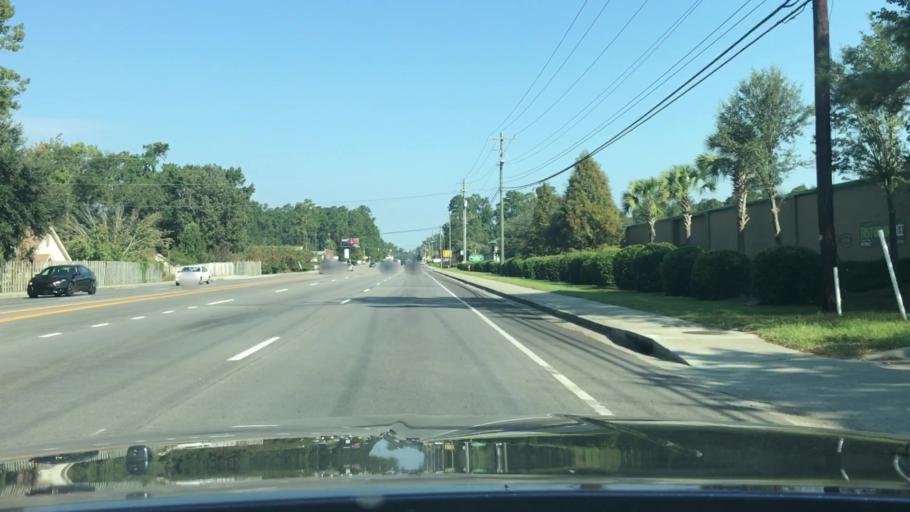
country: US
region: South Carolina
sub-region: Dorchester County
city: Centerville
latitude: 32.9799
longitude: -80.1740
